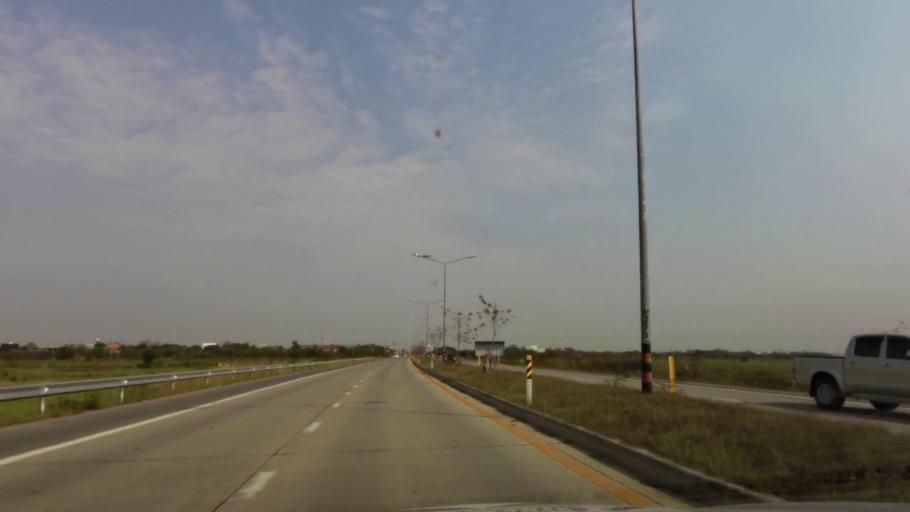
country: TH
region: Phra Nakhon Si Ayutthaya
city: Phra Nakhon Si Ayutthaya
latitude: 14.3332
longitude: 100.5946
